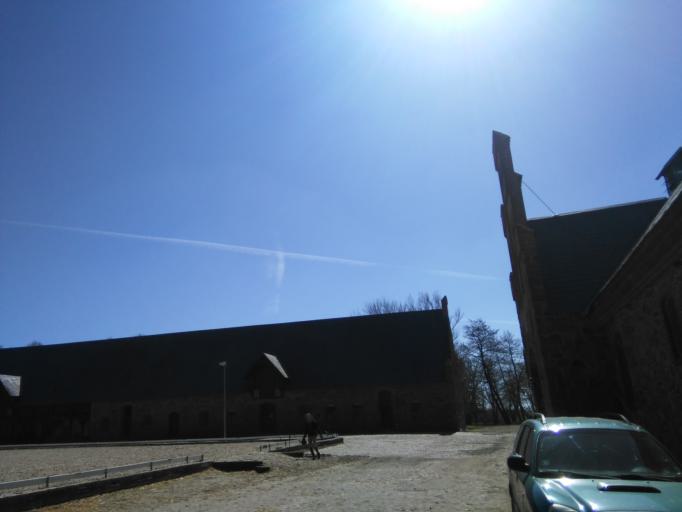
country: DK
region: Central Jutland
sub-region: Arhus Kommune
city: Marslet
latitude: 56.0670
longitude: 10.1860
